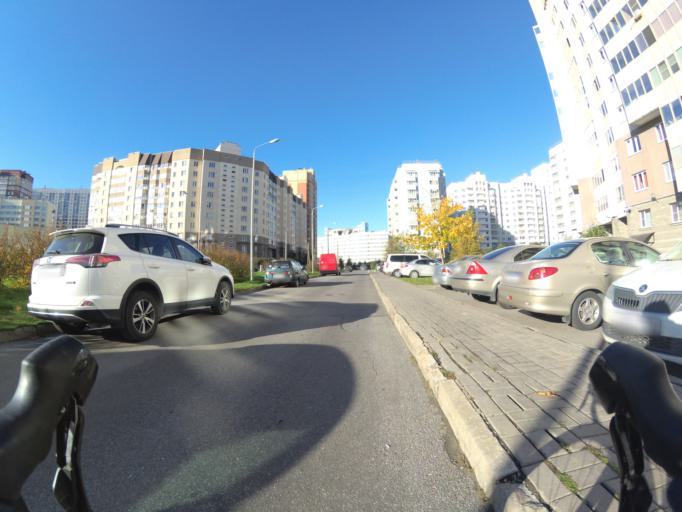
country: RU
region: Leningrad
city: Untolovo
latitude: 60.0003
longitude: 30.2044
